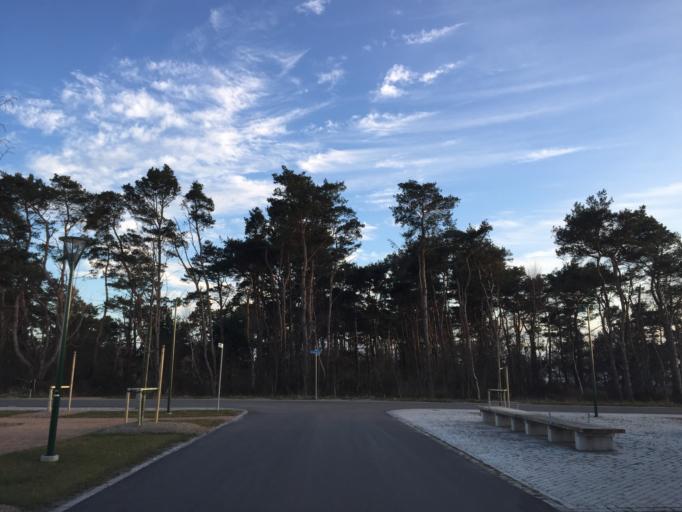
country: SE
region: Skane
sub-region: Vellinge Kommun
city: Skanor med Falsterbo
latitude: 55.4135
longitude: 12.8615
